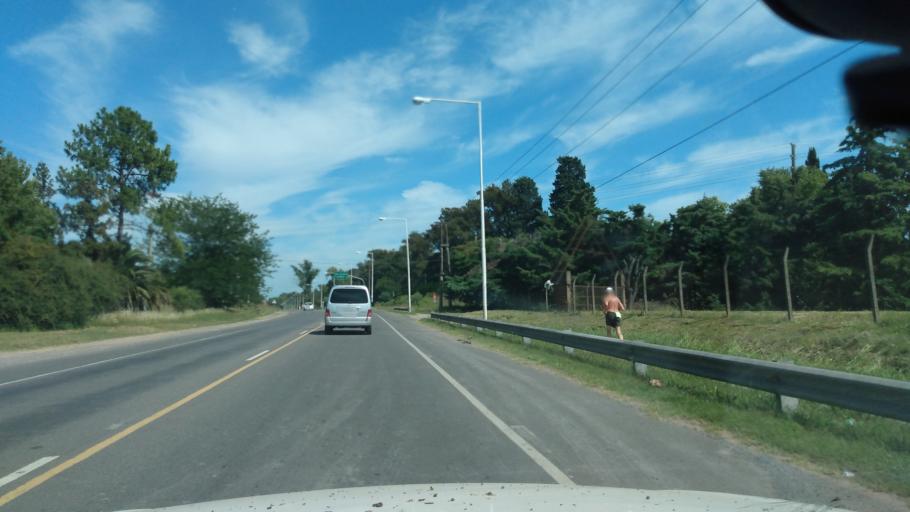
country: AR
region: Buenos Aires
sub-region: Partido de Lujan
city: Lujan
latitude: -34.5493
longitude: -59.1377
